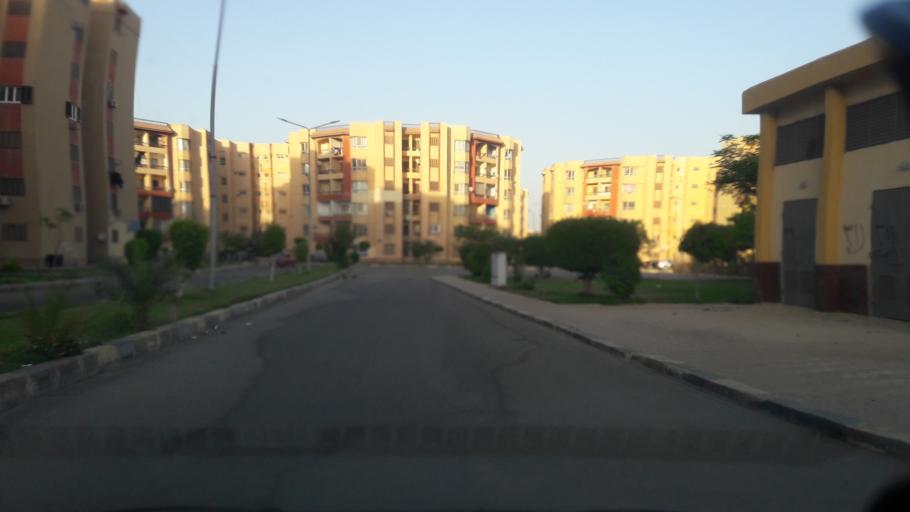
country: EG
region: Al Jizah
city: Madinat Sittah Uktubar
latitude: 29.9555
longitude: 31.0450
